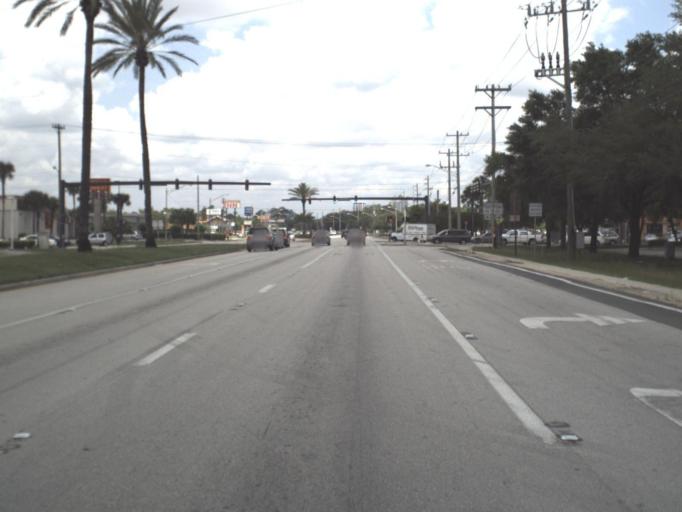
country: US
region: Florida
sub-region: Duval County
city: Jacksonville
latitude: 30.2868
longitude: -81.6328
